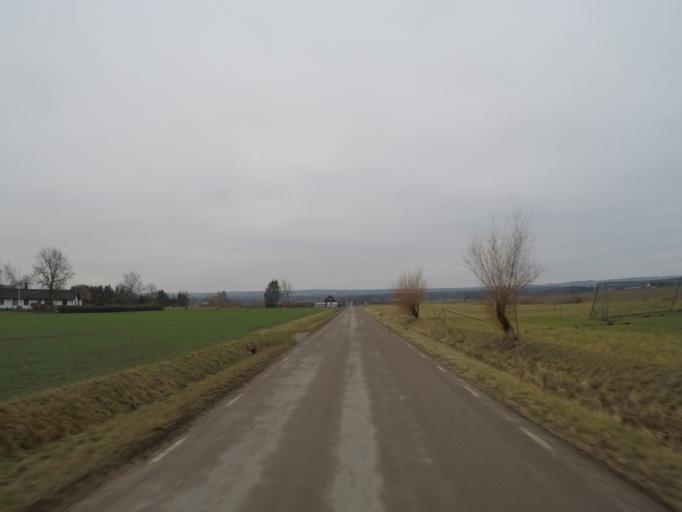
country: SE
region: Skane
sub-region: Hoors Kommun
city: Loberod
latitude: 55.7539
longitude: 13.4218
